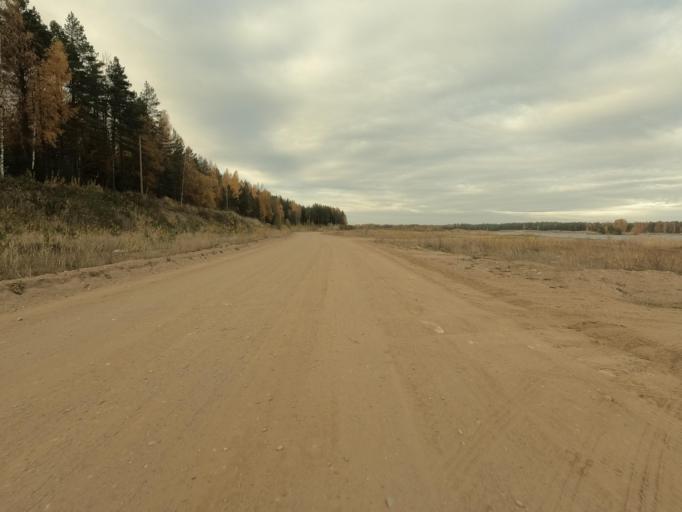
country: RU
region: Leningrad
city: Priladozhskiy
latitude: 59.7010
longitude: 31.3627
